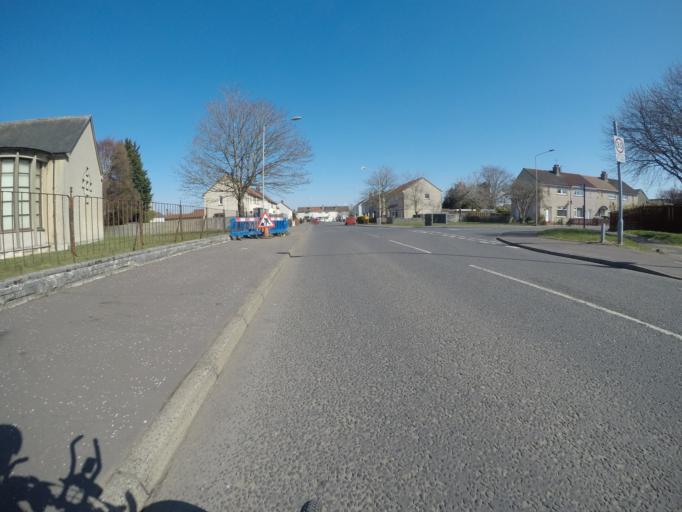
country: GB
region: Scotland
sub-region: North Ayrshire
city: Irvine
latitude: 55.6239
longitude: -4.6604
